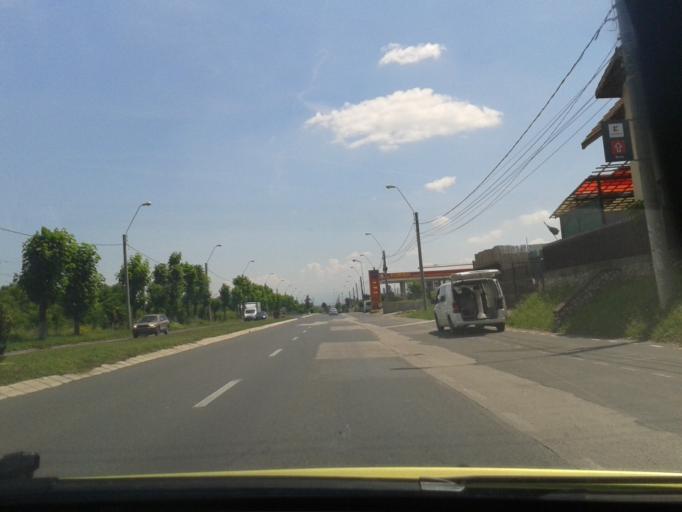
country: RO
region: Hunedoara
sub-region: Municipiul Deva
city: Deva
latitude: 45.8998
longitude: 22.8895
